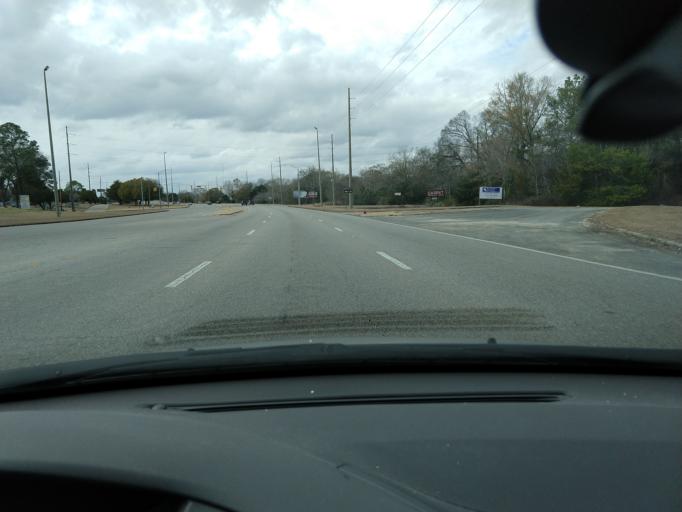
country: US
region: Alabama
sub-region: Houston County
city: Dothan
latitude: 31.2222
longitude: -85.3730
